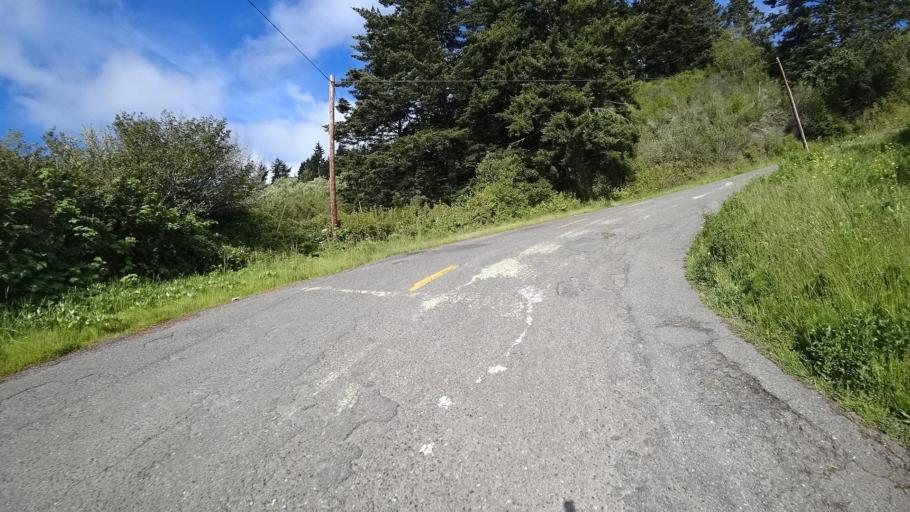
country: US
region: California
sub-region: Humboldt County
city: Ferndale
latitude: 40.4577
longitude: -124.3707
